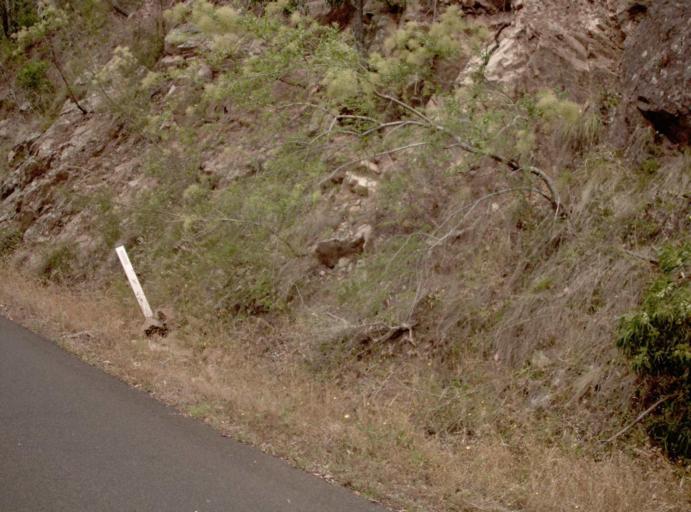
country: AU
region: Victoria
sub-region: Wellington
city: Heyfield
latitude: -37.7036
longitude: 146.6679
